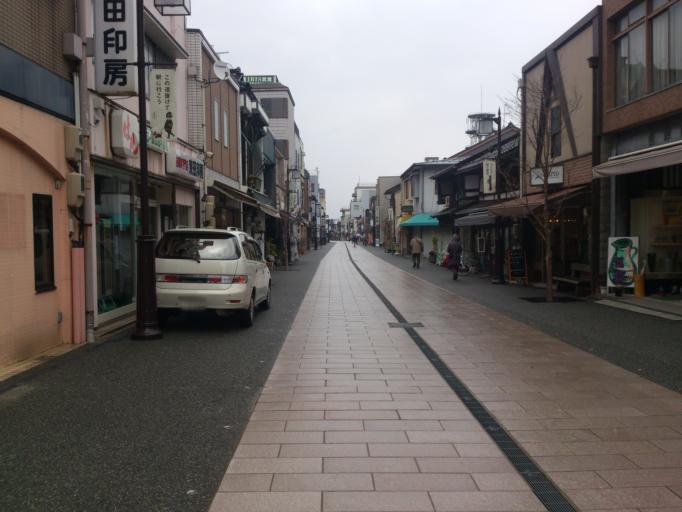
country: JP
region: Ishikawa
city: Kanazawa-shi
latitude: 36.5731
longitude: 136.6552
